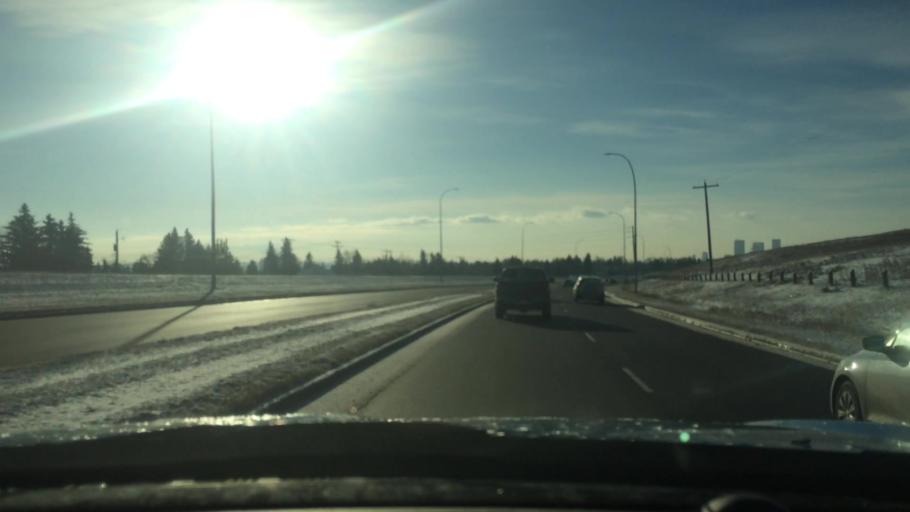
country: CA
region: Alberta
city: Calgary
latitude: 51.1156
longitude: -114.0848
